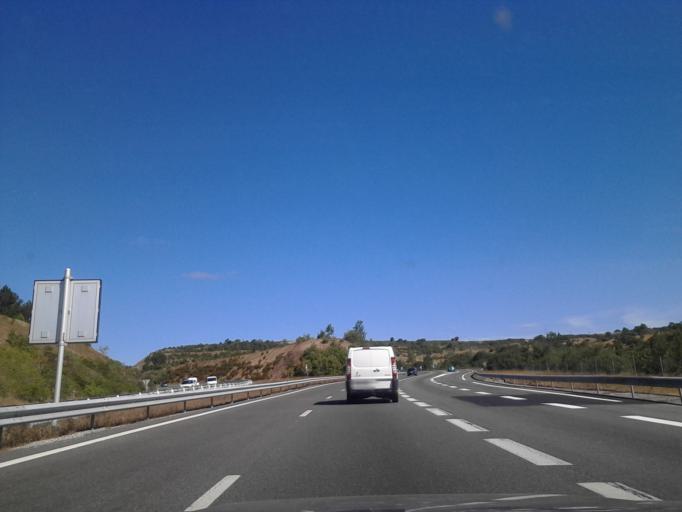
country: FR
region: Languedoc-Roussillon
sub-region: Departement de l'Herault
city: Lodeve
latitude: 43.8435
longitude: 3.3125
